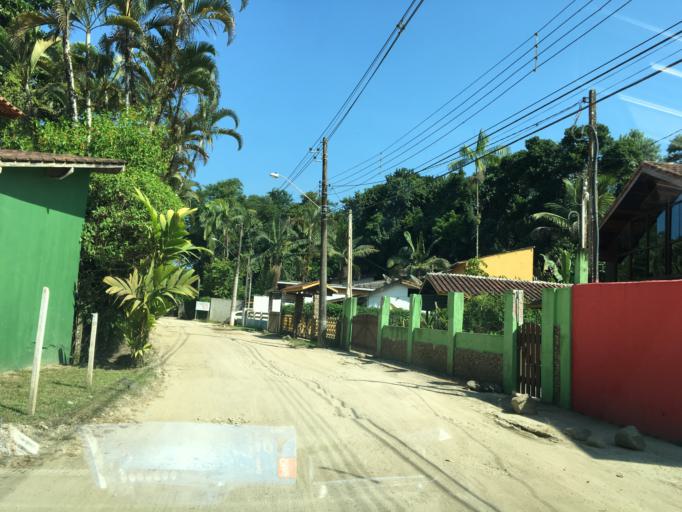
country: BR
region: Sao Paulo
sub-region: Ubatuba
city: Ubatuba
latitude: -23.4006
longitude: -45.0141
